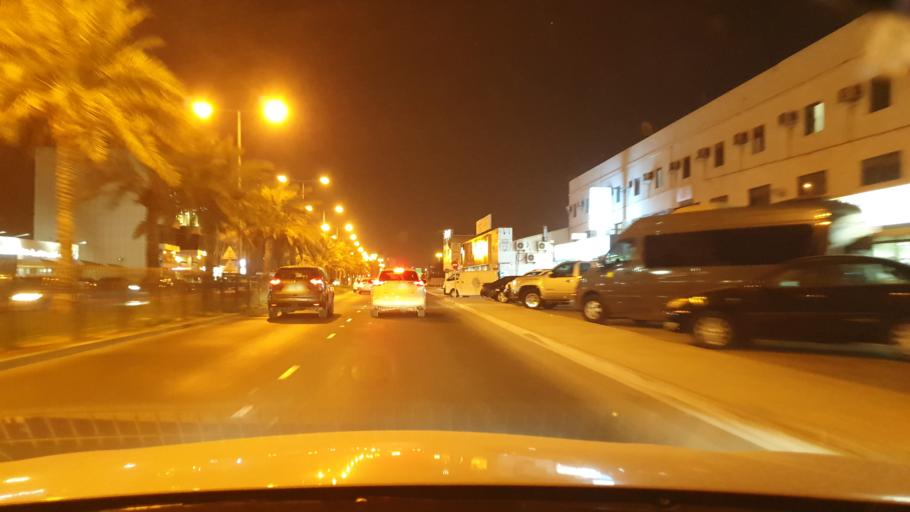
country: BH
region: Manama
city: Jidd Hafs
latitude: 26.2197
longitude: 50.4951
